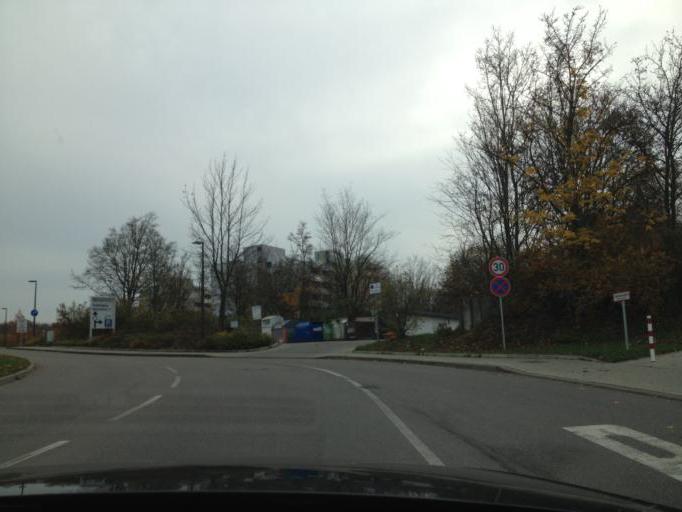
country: DE
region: Baden-Wuerttemberg
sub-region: Regierungsbezirk Stuttgart
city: Neckarsulm
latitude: 49.2121
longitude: 9.2344
